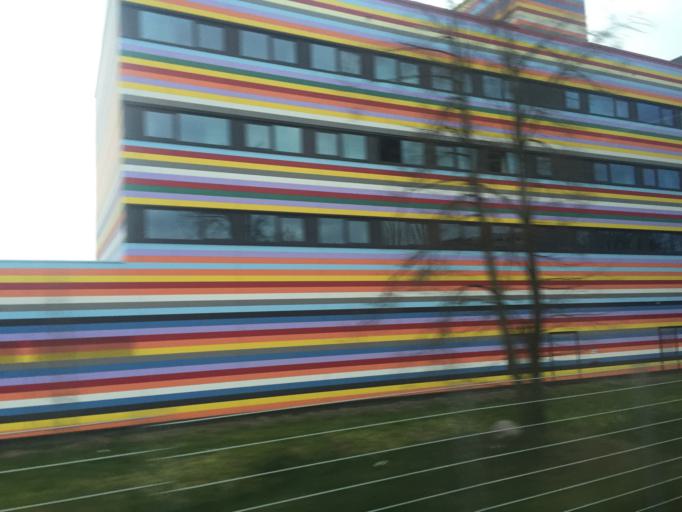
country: DE
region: Berlin
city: Altglienicke
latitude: 52.3973
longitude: 13.5410
